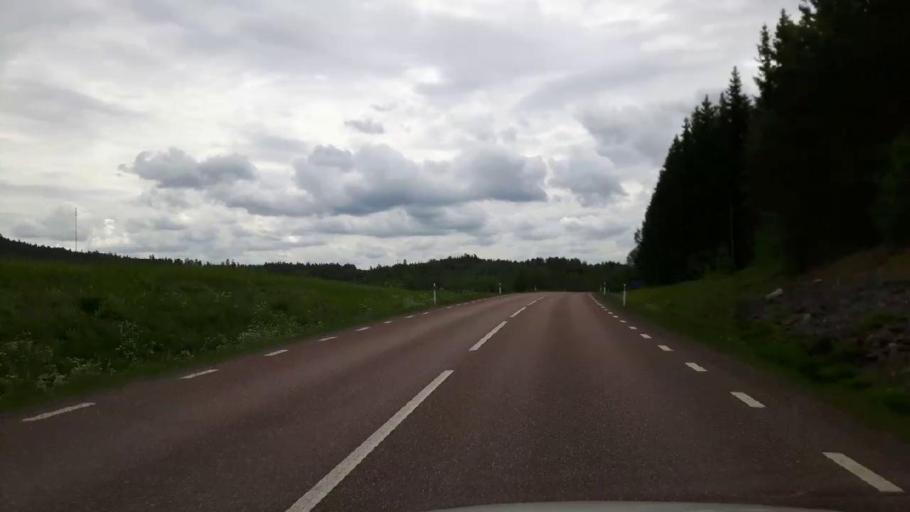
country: SE
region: Dalarna
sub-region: Hedemora Kommun
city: Brunna
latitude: 60.2159
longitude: 15.9916
